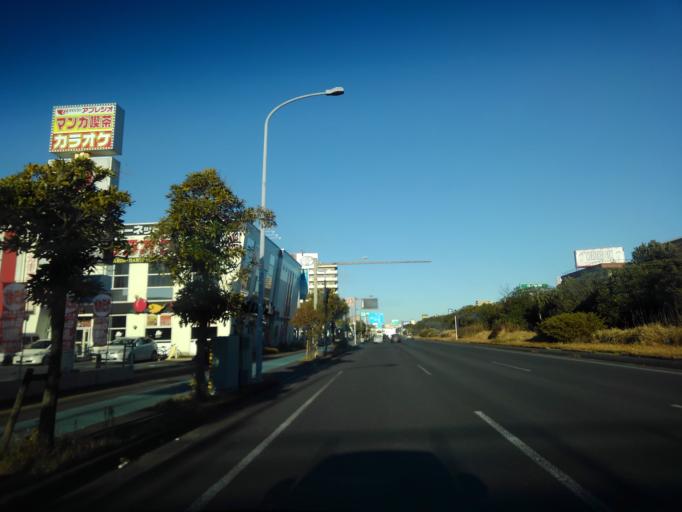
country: JP
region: Chiba
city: Funabashi
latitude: 35.6596
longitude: 140.0479
